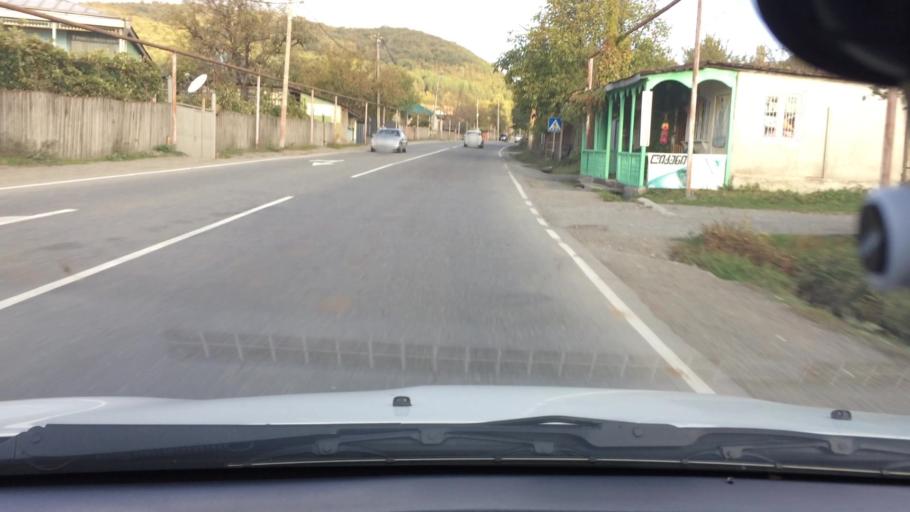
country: GE
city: Surami
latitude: 42.0309
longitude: 43.5250
